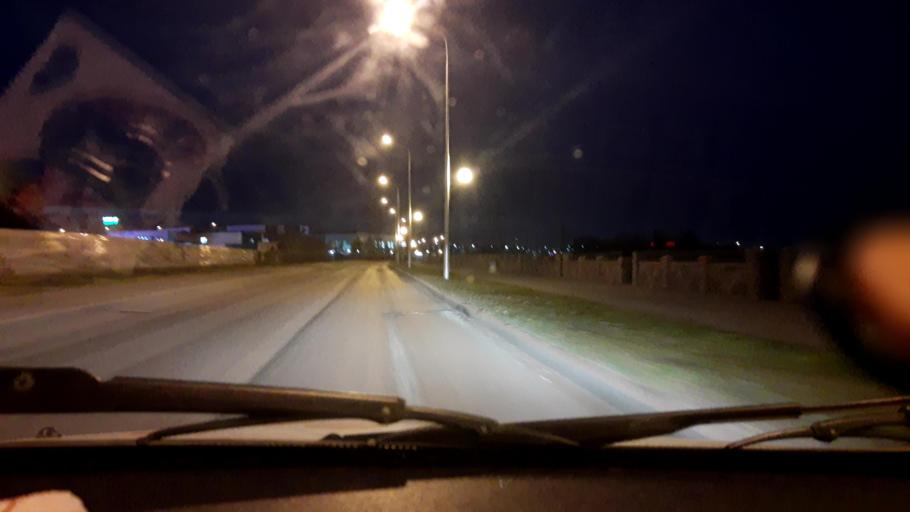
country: RU
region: Bashkortostan
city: Ufa
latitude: 54.7809
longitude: 56.0777
